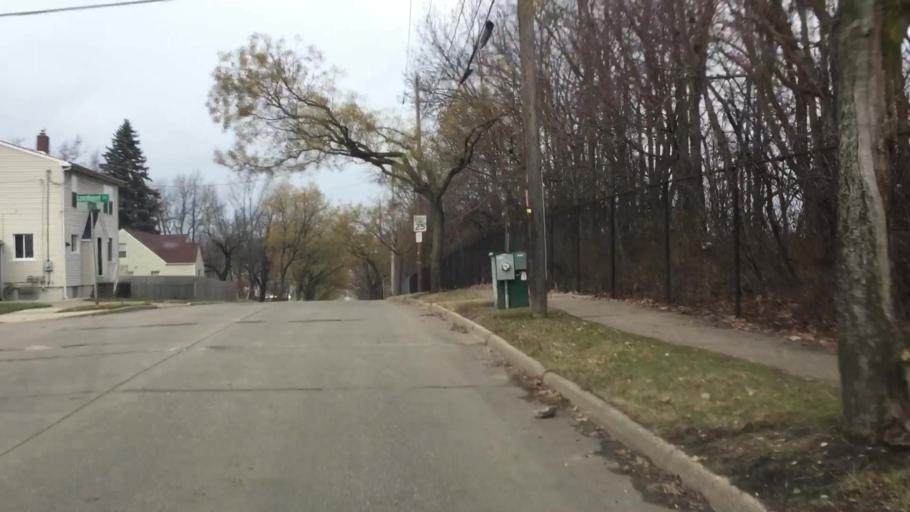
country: US
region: Ohio
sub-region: Summit County
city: Cuyahoga Falls
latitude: 41.1089
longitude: -81.5021
